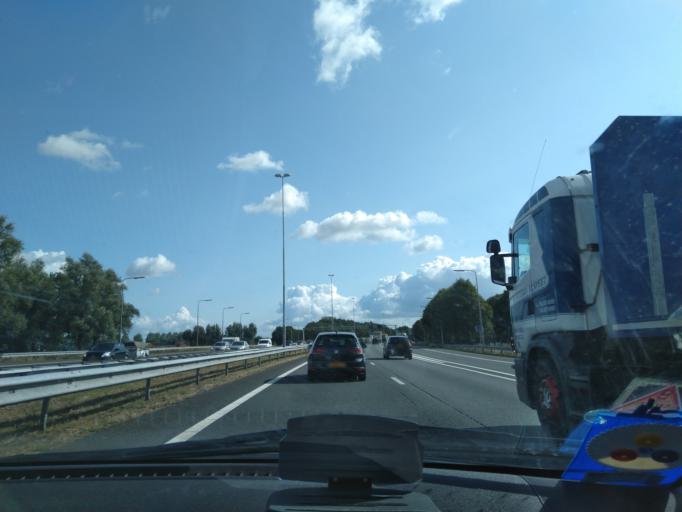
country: NL
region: Utrecht
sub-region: Gemeente IJsselstein
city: IJsselstein
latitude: 51.9535
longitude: 5.0198
